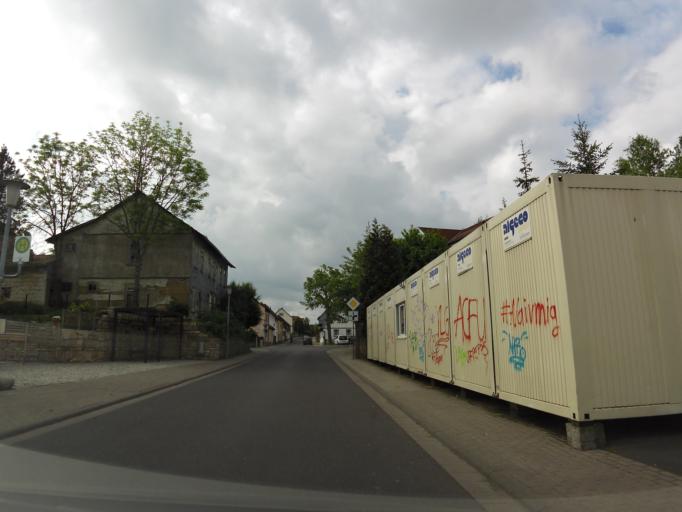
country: DE
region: Thuringia
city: Horselgau
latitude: 50.9205
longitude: 10.5850
